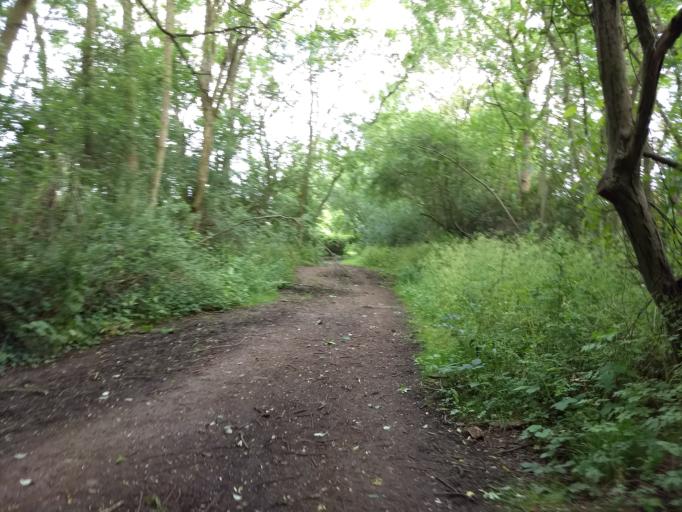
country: GB
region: England
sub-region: Milton Keynes
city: Shenley Church End
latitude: 52.0018
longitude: -0.8089
